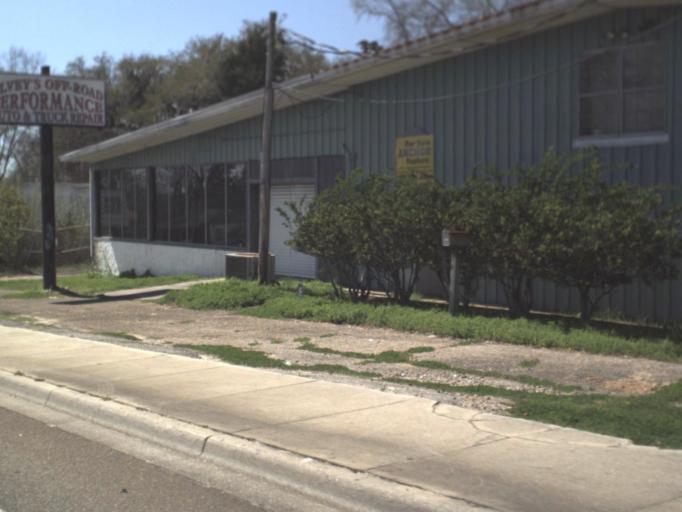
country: US
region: Florida
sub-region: Leon County
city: Tallahassee
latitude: 30.4195
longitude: -84.2807
